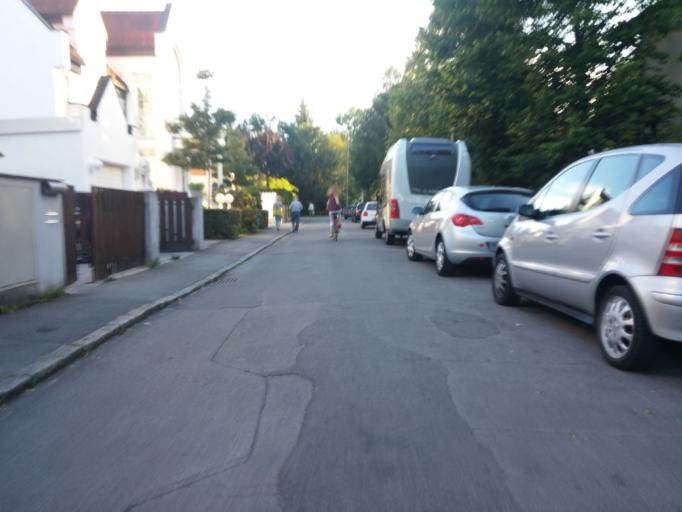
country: DE
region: Bavaria
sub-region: Upper Bavaria
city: Haar
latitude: 48.1141
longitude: 11.6981
